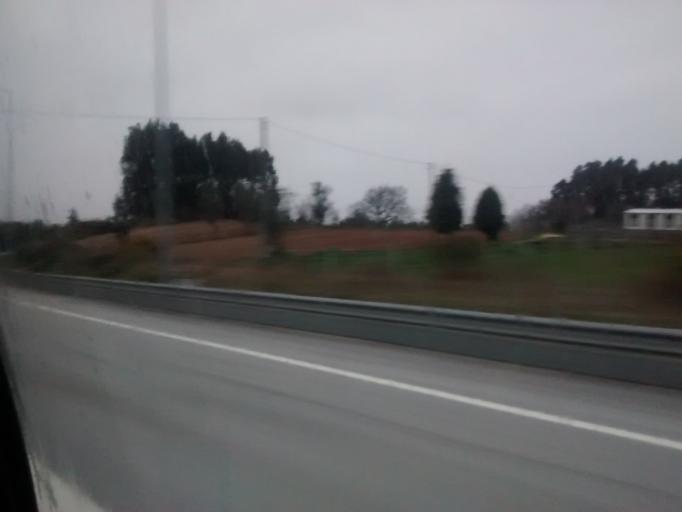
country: PT
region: Aveiro
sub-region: Estarreja
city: Salreu
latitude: 40.6872
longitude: -8.5419
